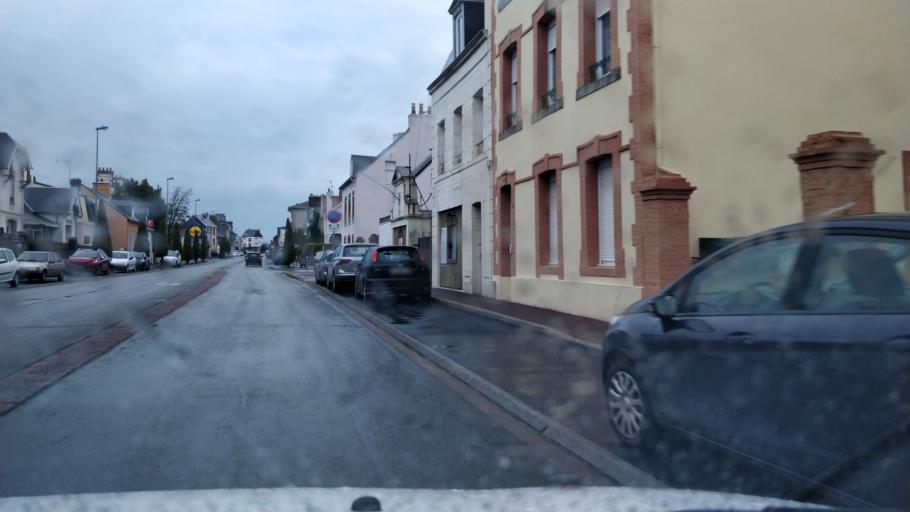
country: FR
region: Lower Normandy
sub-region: Departement de la Manche
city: Donville-les-Bains
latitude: 48.8359
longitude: -1.5803
